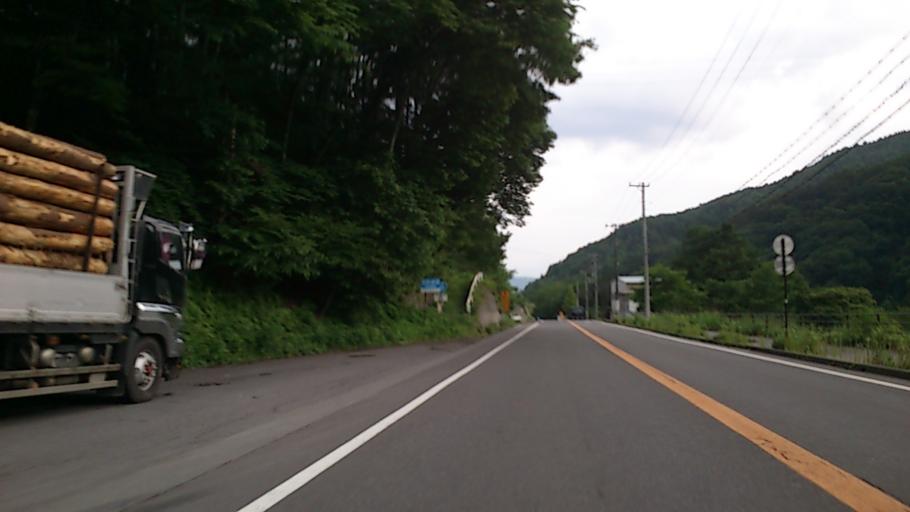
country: JP
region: Nagano
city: Suwa
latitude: 36.1168
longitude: 138.1008
